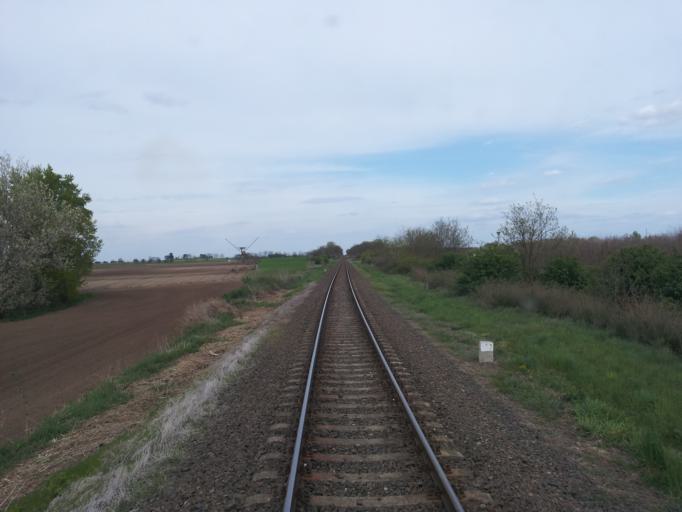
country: HU
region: Komarom-Esztergom
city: Nagyigmand
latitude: 47.6909
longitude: 18.0692
